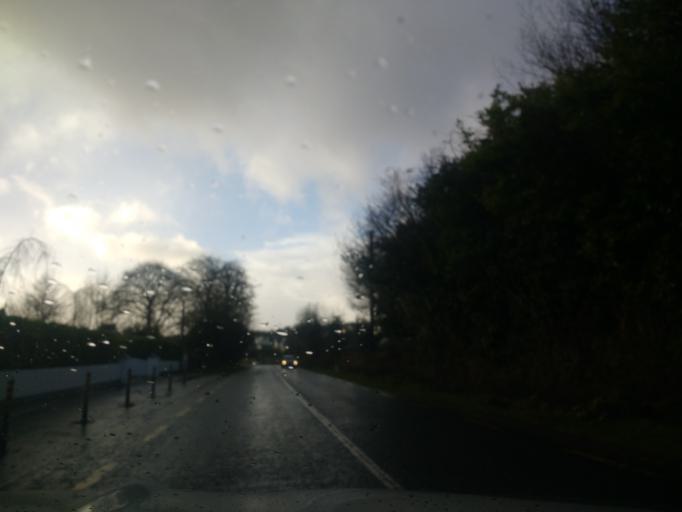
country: IE
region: Ulster
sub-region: County Donegal
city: Letterkenny
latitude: 54.9736
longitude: -7.6867
